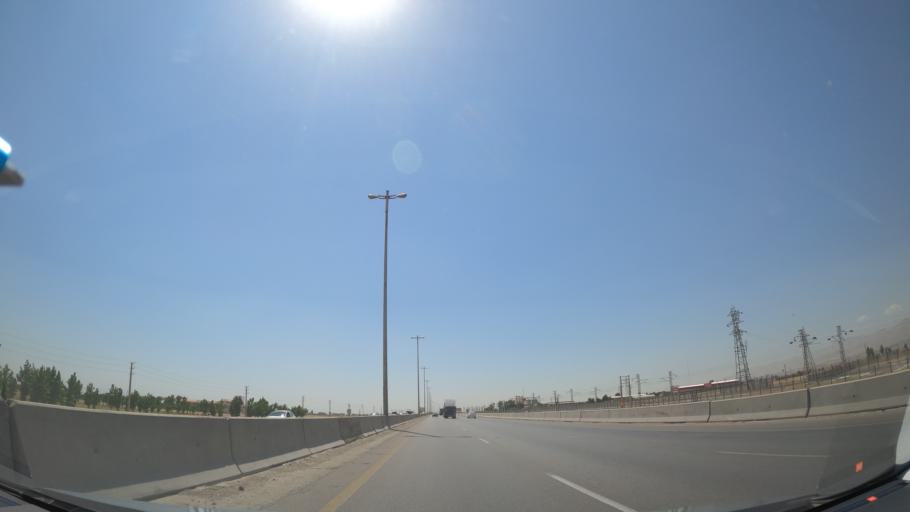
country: IR
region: Alborz
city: Hashtgerd
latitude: 35.9154
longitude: 50.8047
